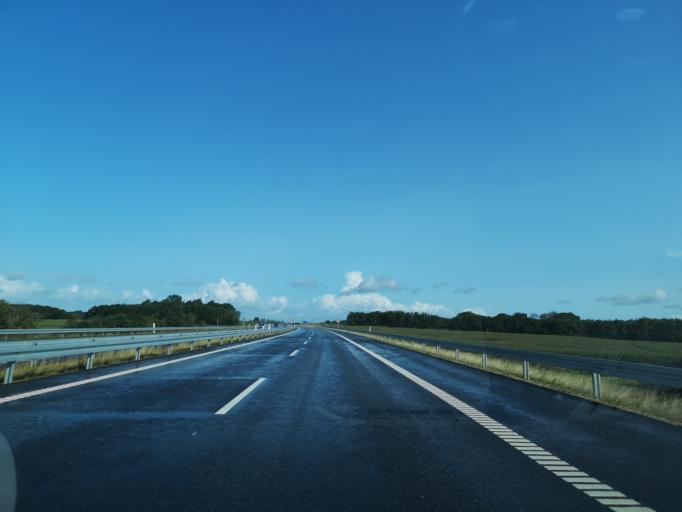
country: DK
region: Central Jutland
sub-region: Herning Kommune
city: Snejbjerg
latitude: 56.1776
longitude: 8.8927
